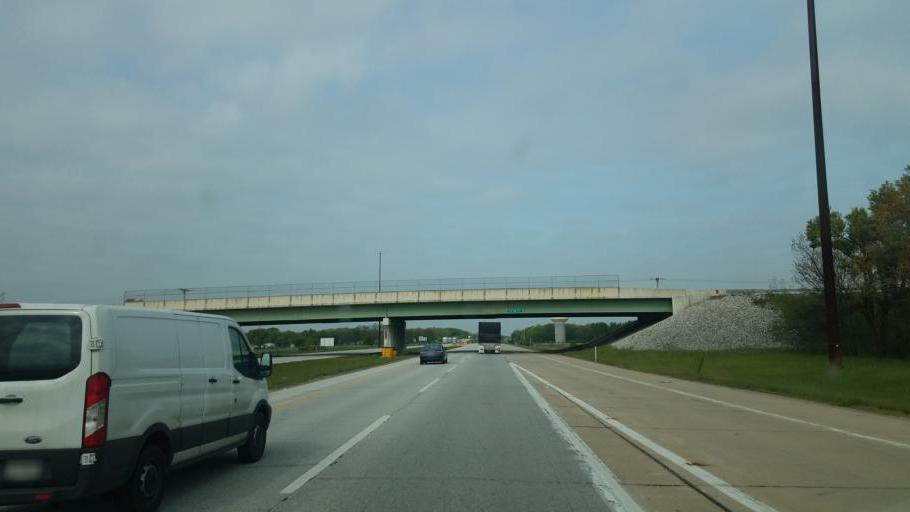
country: US
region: Indiana
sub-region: Elkhart County
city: Bristol
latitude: 41.7305
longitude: -85.8871
